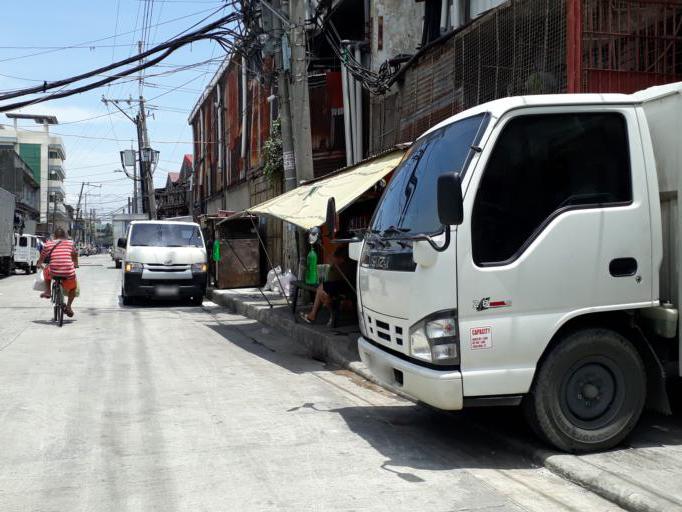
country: PH
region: Metro Manila
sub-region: Caloocan City
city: Niugan
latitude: 14.6465
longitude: 120.9816
